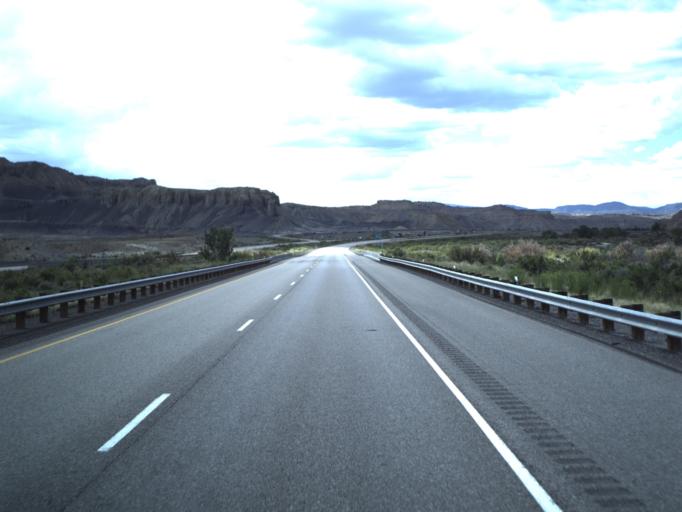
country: US
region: Utah
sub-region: Emery County
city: Ferron
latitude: 38.8138
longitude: -111.1992
